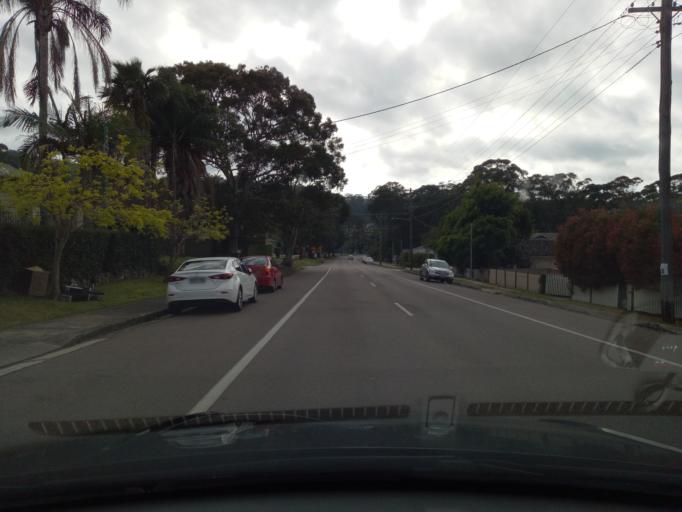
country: AU
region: New South Wales
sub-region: Gosford Shire
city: East Gosford
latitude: -33.4325
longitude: 151.3561
